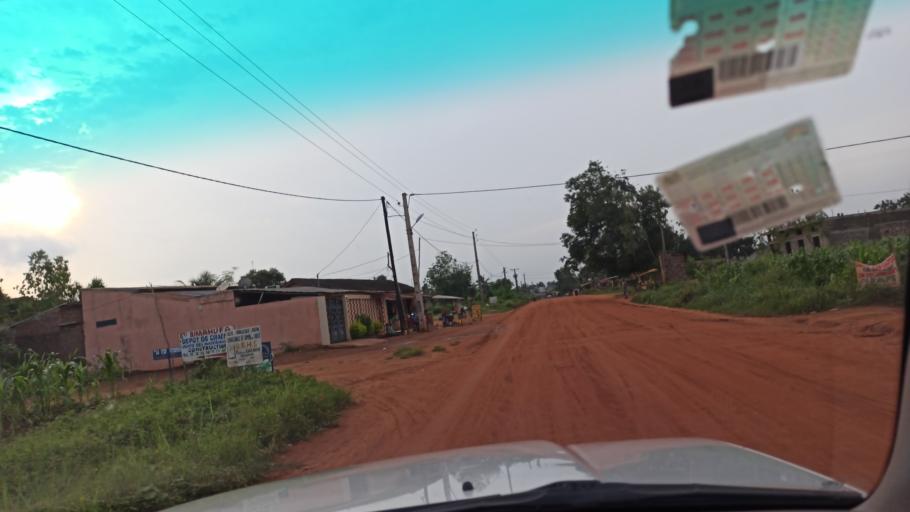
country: BJ
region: Queme
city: Porto-Novo
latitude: 6.5158
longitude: 2.6813
